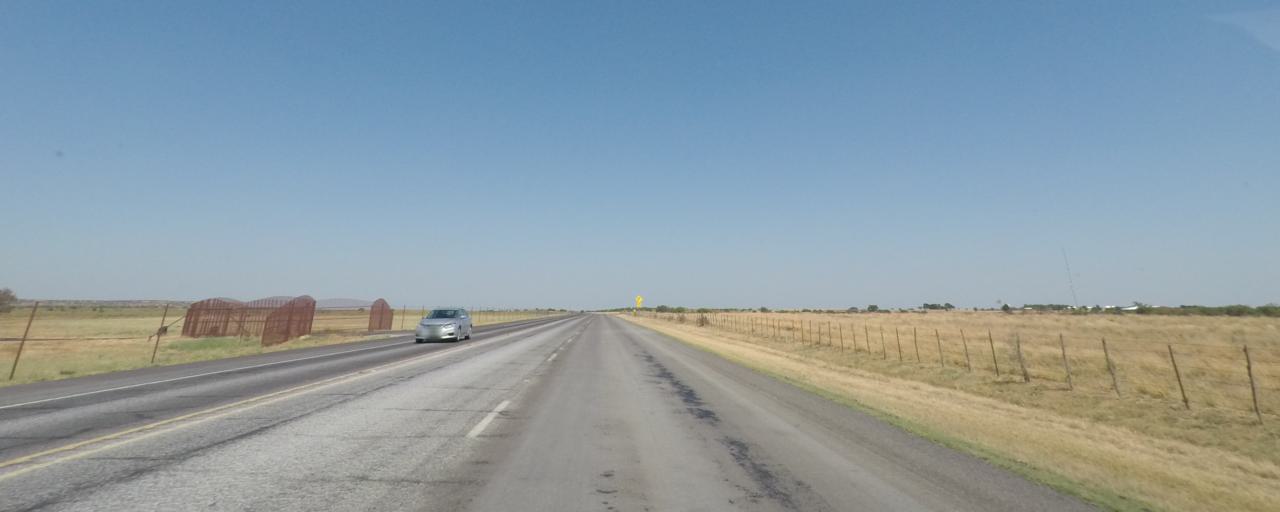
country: US
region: Texas
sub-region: King County
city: Guthrie
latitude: 33.6332
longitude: -100.3497
